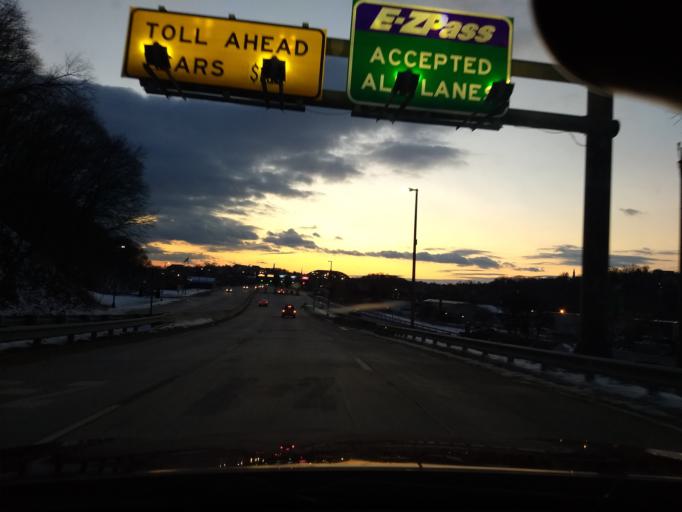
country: US
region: New Jersey
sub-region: Warren County
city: Phillipsburg
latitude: 40.6964
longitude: -75.1972
